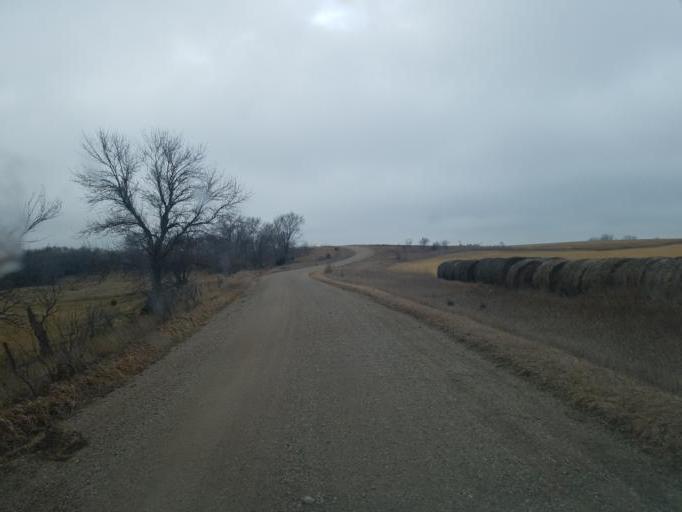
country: US
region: Nebraska
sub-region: Knox County
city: Center
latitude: 42.5475
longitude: -97.7997
